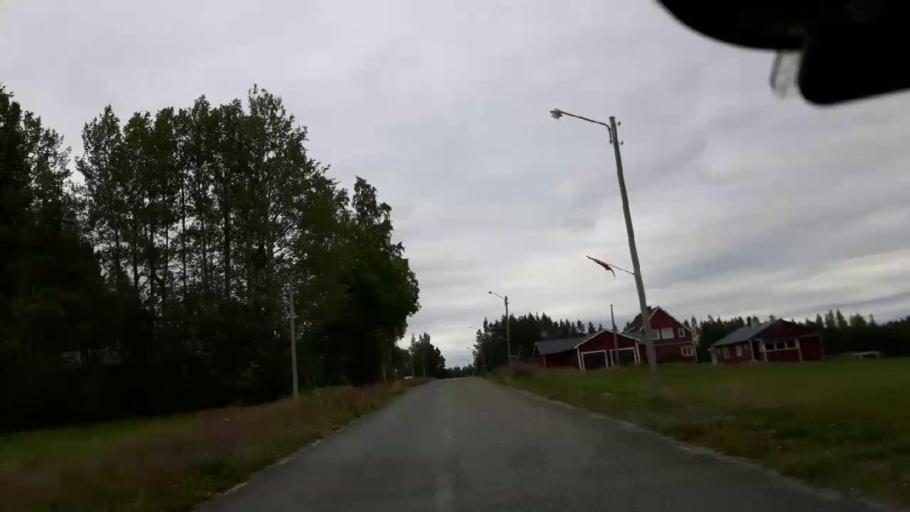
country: SE
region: Jaemtland
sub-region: Braecke Kommun
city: Braecke
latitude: 62.8392
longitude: 15.6812
